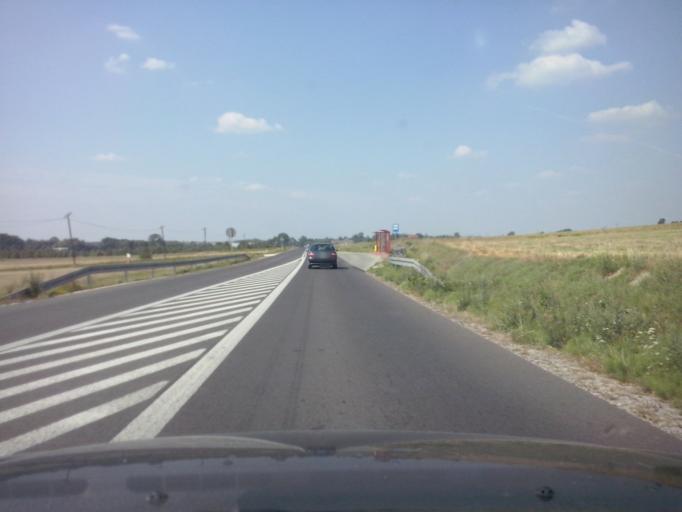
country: PL
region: Swietokrzyskie
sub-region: Powiat buski
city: Gnojno
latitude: 50.5876
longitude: 20.9053
